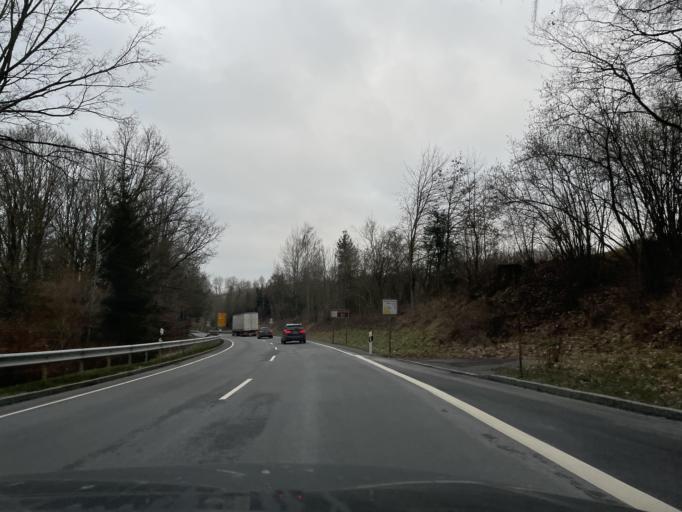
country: DE
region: Bavaria
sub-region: Upper Palatinate
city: Miltach
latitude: 49.1624
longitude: 12.7597
